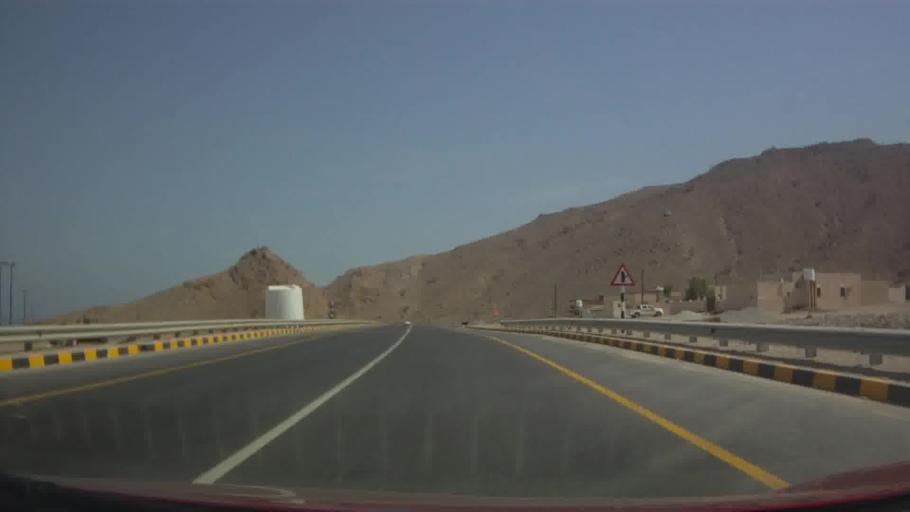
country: OM
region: Muhafazat Masqat
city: Muscat
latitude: 23.3897
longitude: 58.8005
